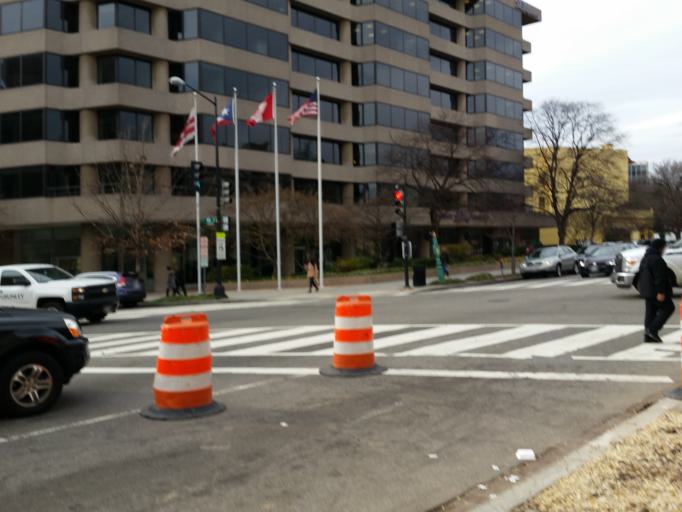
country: US
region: Washington, D.C.
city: Washington, D.C.
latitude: 38.9088
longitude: -77.0415
